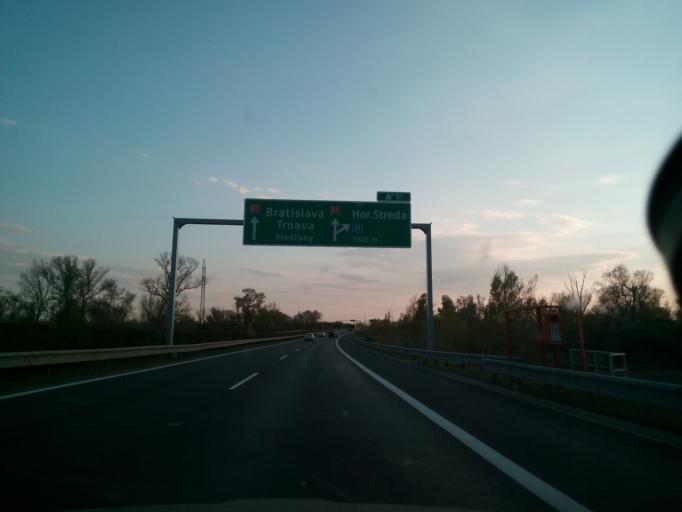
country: SK
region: Trnavsky
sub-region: Okres Trnava
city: Piestany
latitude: 48.6567
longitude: 17.8639
